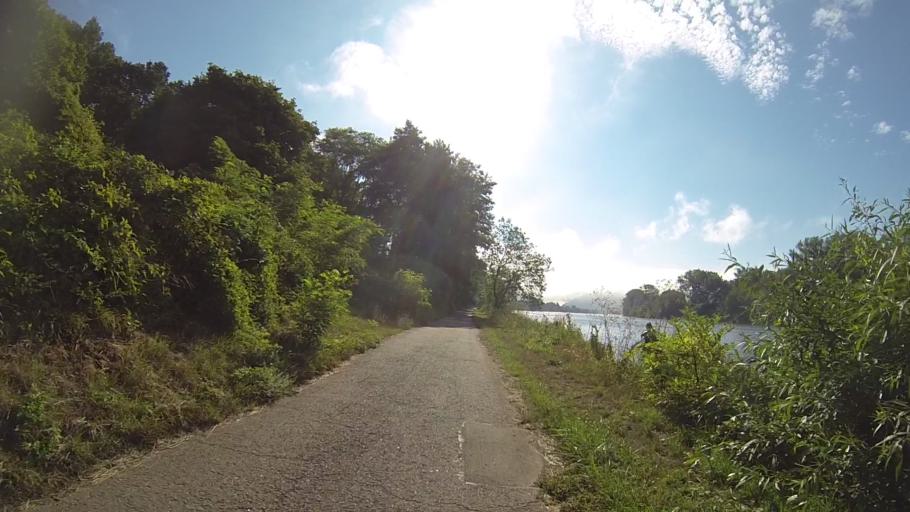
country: DE
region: Rheinland-Pfalz
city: Kenn
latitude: 49.8222
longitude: 6.7201
